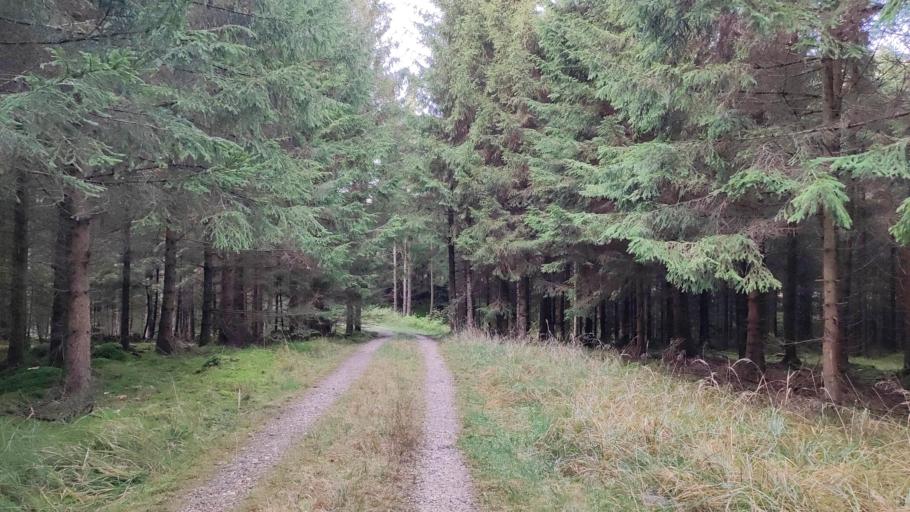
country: DE
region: Bavaria
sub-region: Swabia
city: Welden
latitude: 48.4390
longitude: 10.6320
